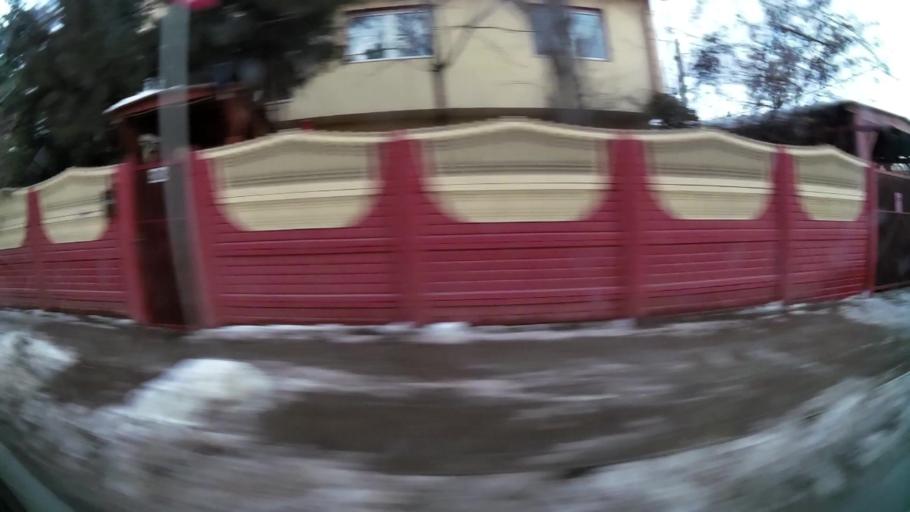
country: RO
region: Ilfov
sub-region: Comuna Popesti-Leordeni
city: Popesti-Leordeni
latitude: 44.3769
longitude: 26.1574
